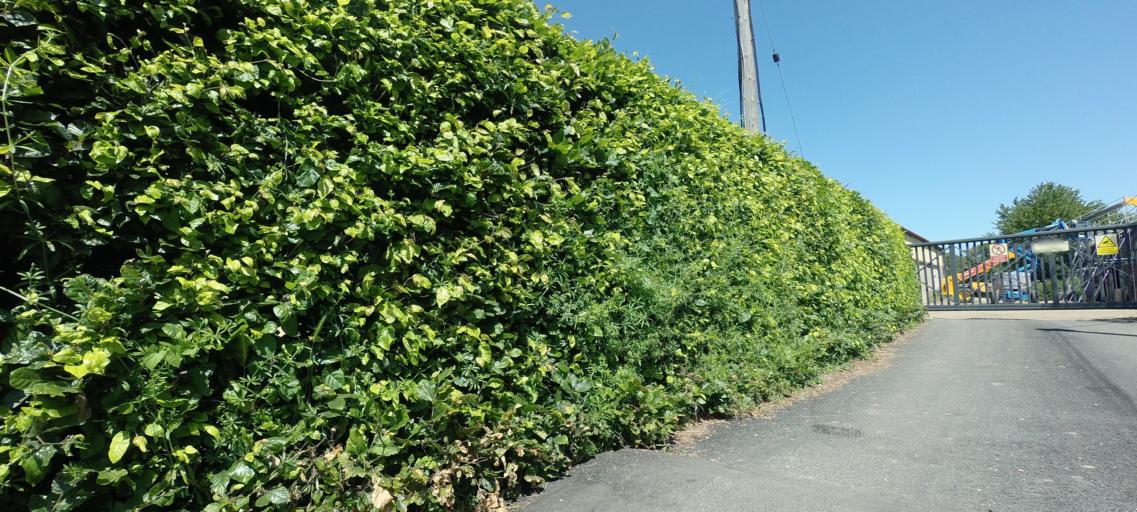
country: GB
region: England
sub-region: Kent
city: Eynsford
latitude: 51.3697
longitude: 0.2112
